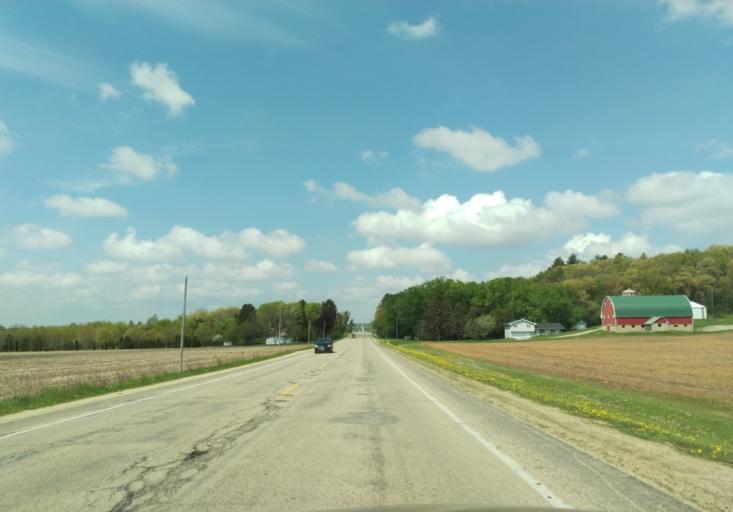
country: US
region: Wisconsin
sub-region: Dane County
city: Cross Plains
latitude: 43.0605
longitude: -89.6178
